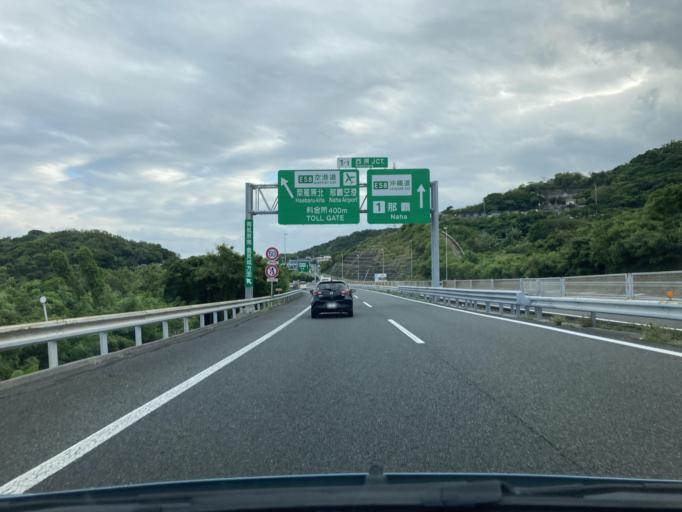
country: JP
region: Okinawa
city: Ginowan
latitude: 26.2252
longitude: 127.7382
